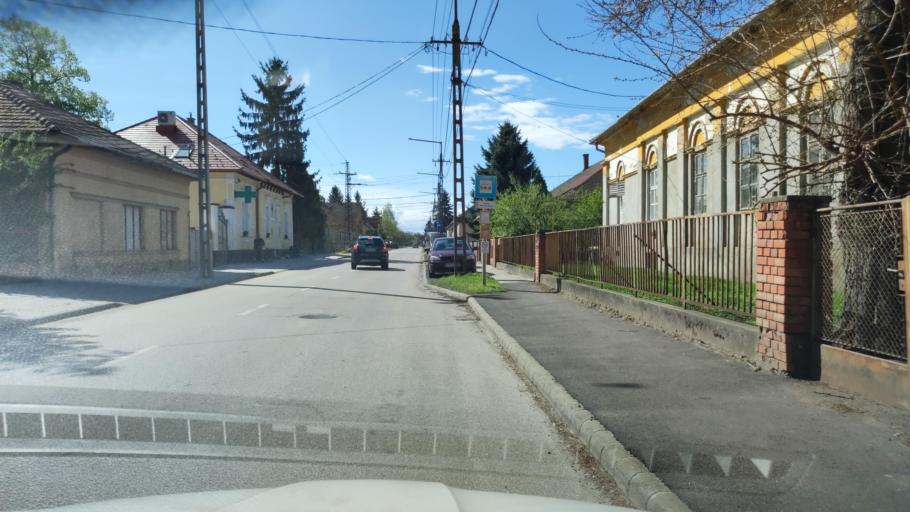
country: HU
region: Pest
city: Abony
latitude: 47.1849
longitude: 20.0050
